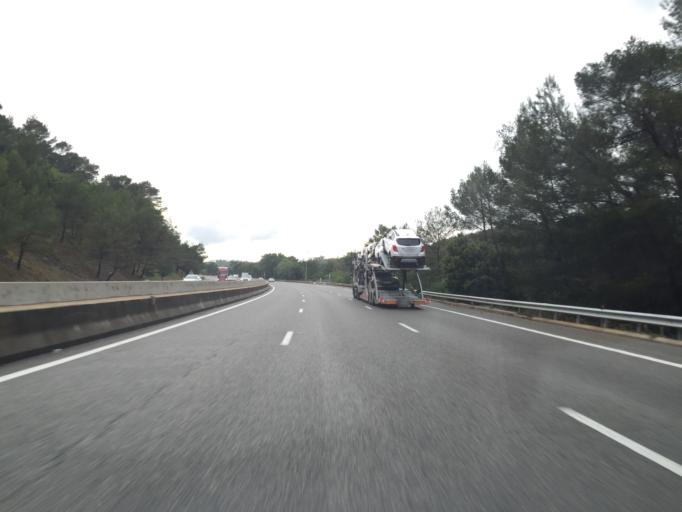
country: FR
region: Provence-Alpes-Cote d'Azur
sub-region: Departement du Var
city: Cabasse
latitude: 43.4092
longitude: 6.1802
